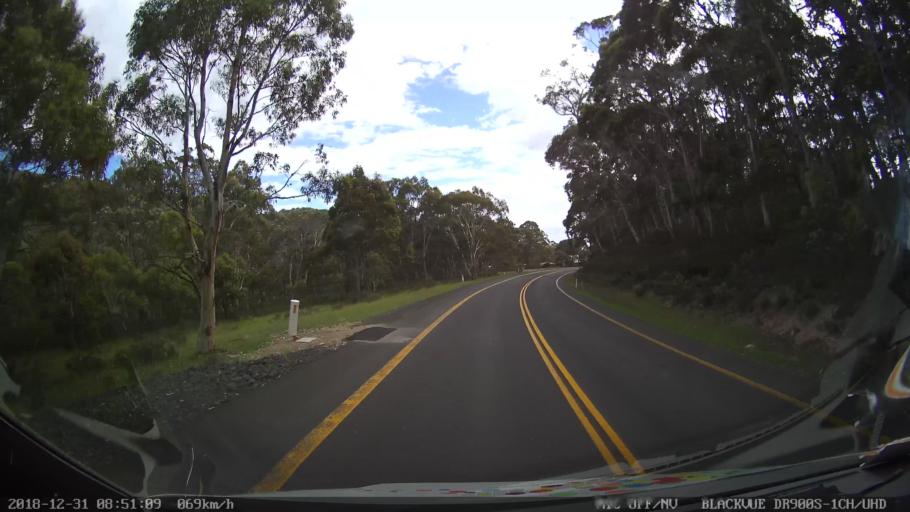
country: AU
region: New South Wales
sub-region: Snowy River
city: Jindabyne
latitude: -36.3481
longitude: 148.5240
